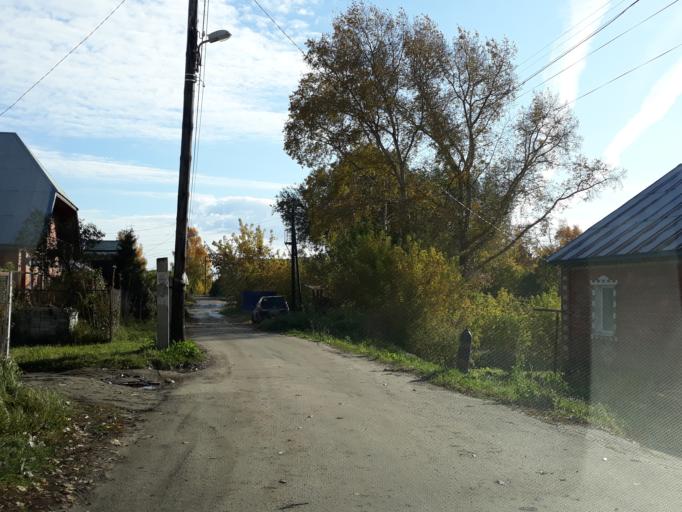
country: RU
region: Nizjnij Novgorod
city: Afonino
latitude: 56.2332
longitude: 44.0203
